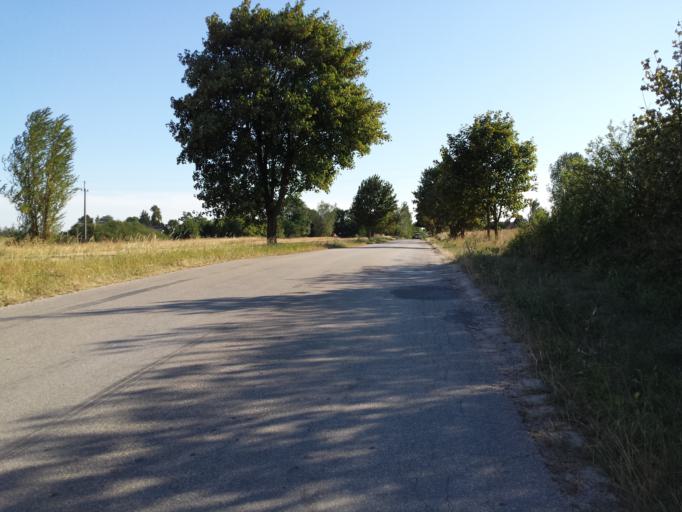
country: PL
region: Swietokrzyskie
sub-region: Powiat buski
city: Gnojno
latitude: 50.6508
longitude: 20.8210
